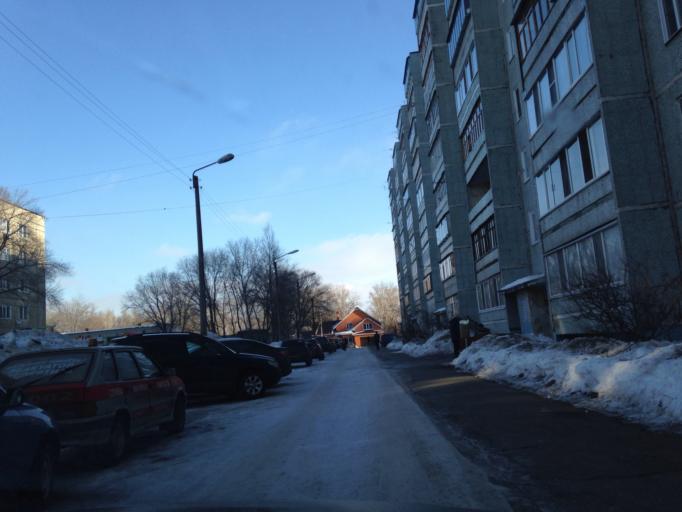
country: RU
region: Ulyanovsk
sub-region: Ulyanovskiy Rayon
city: Ulyanovsk
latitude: 54.3383
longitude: 48.5436
